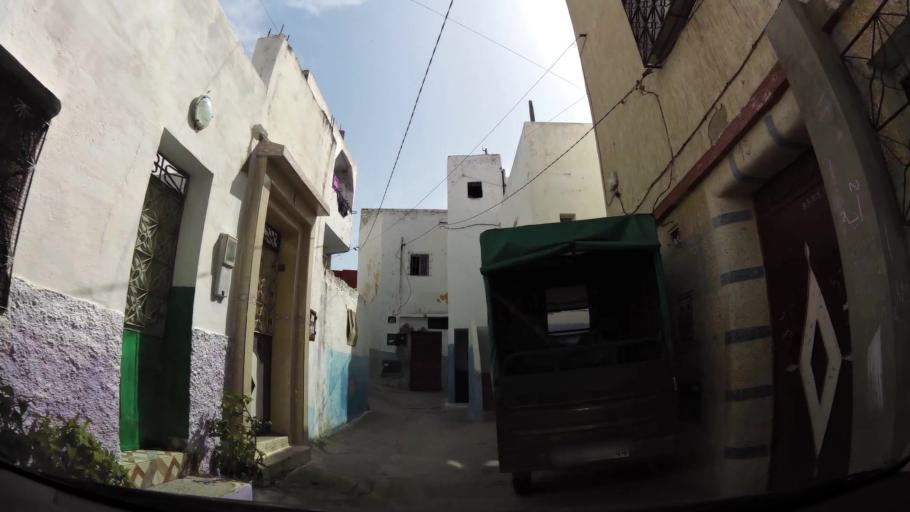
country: MA
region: Tanger-Tetouan
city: Tetouan
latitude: 35.5762
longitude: -5.3834
